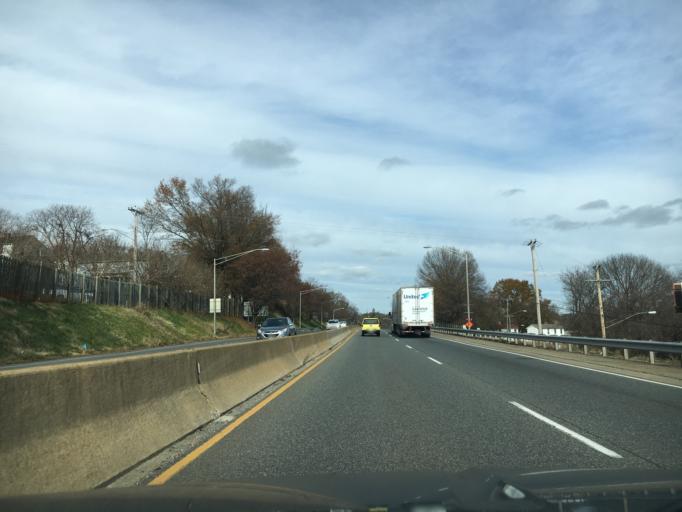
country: US
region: Virginia
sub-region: City of Lynchburg
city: West Lynchburg
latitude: 37.3942
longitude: -79.1572
